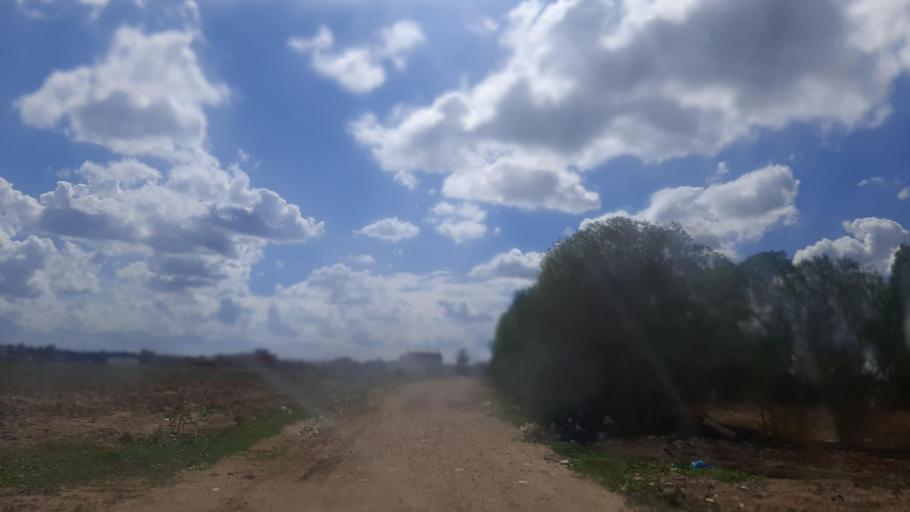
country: TN
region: Nabul
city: Korba
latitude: 36.5981
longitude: 10.8564
